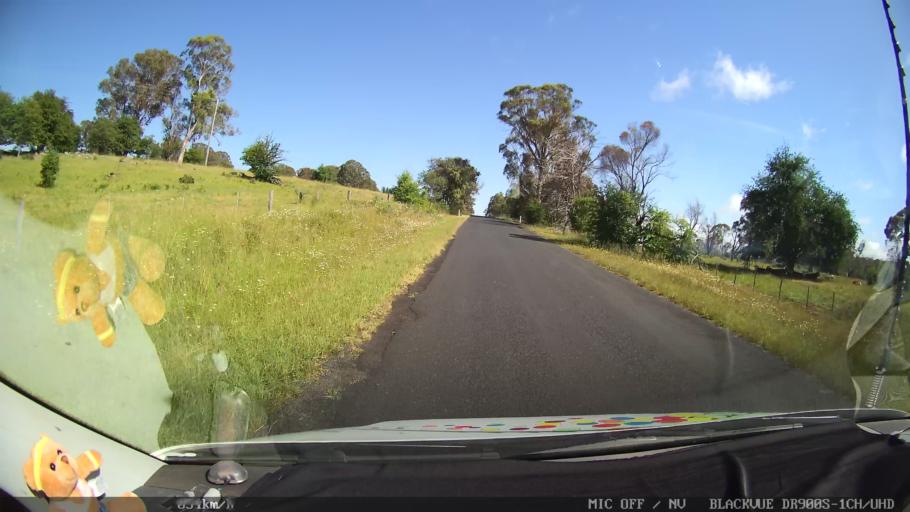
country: AU
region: New South Wales
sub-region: Guyra
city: Guyra
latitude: -30.1057
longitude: 151.6792
